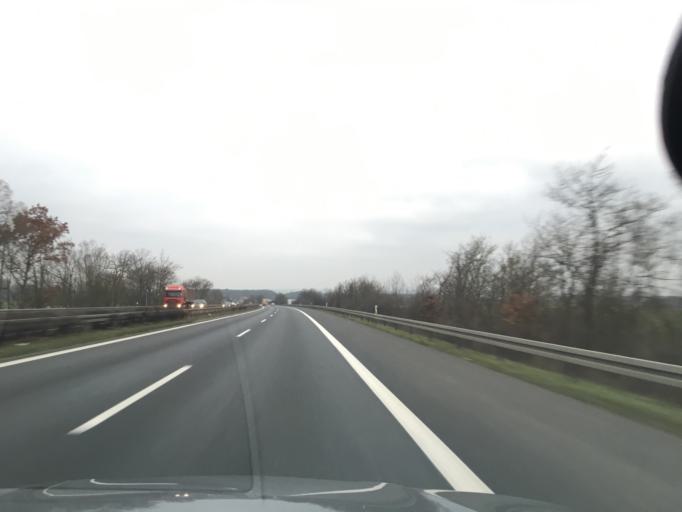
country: DE
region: Bavaria
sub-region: Regierungsbezirk Unterfranken
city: Kleinlangheim
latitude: 49.7799
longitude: 10.2980
